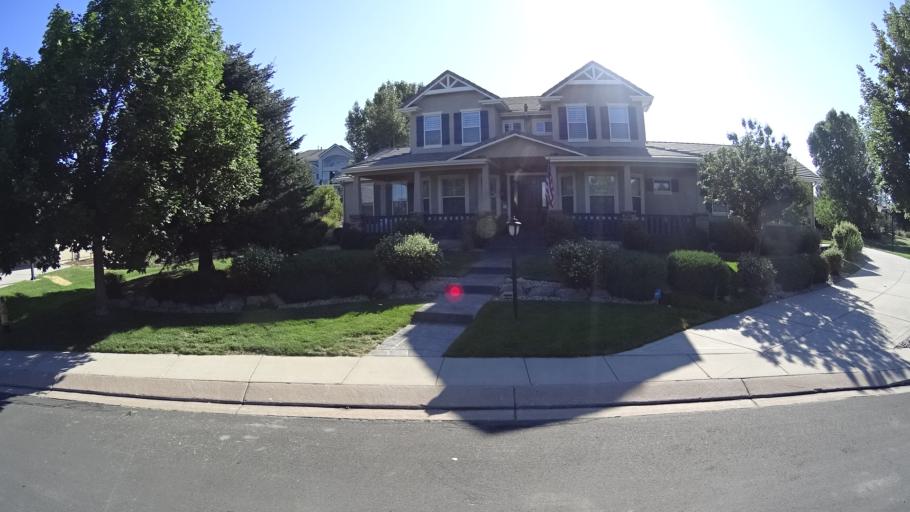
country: US
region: Colorado
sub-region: El Paso County
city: Black Forest
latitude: 38.9738
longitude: -104.7704
